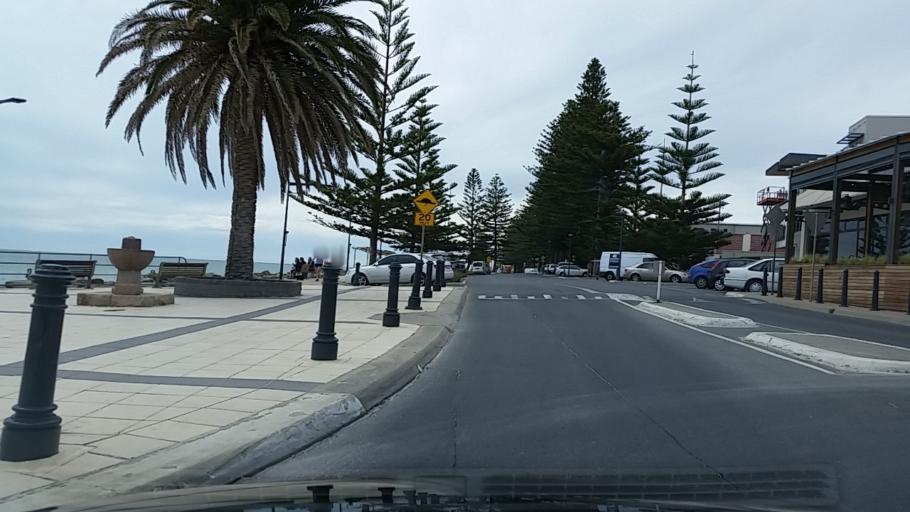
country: AU
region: South Australia
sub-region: Adelaide
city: Brighton
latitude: -35.0173
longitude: 138.5145
